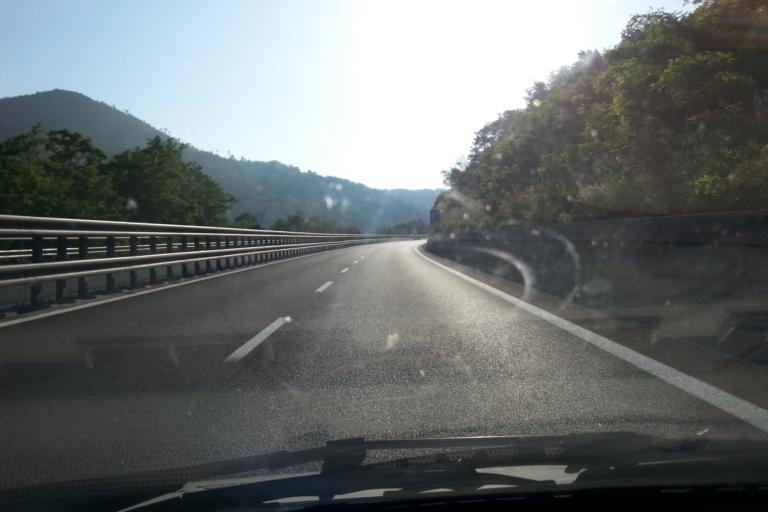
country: IT
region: Liguria
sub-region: Provincia di Savona
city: Vezzi Portio
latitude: 44.2265
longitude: 8.3796
